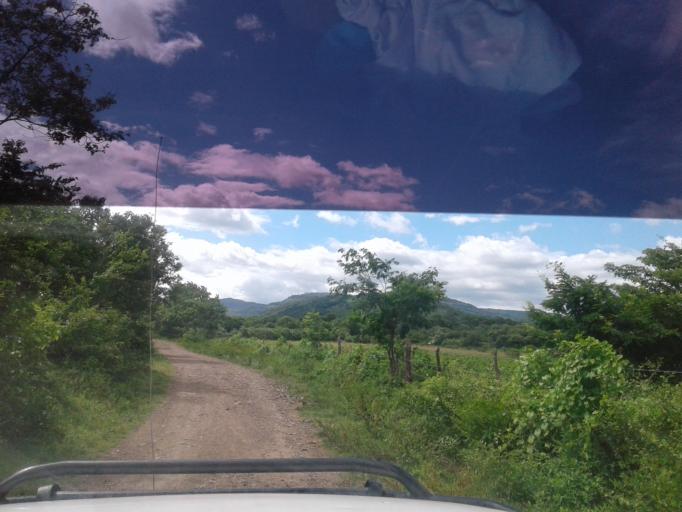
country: NI
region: Matagalpa
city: Ciudad Dario
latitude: 12.8475
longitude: -86.2208
